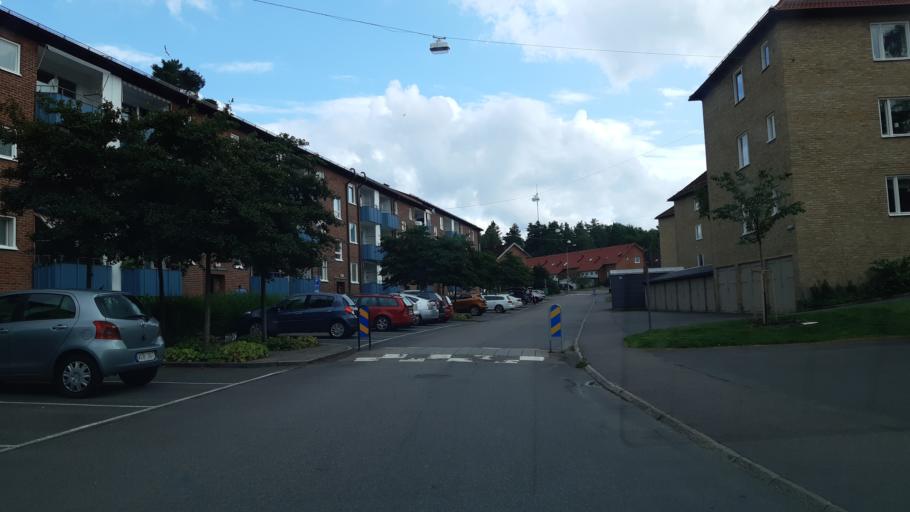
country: SE
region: Vaestra Goetaland
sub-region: Partille Kommun
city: Partille
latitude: 57.7145
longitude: 12.0539
